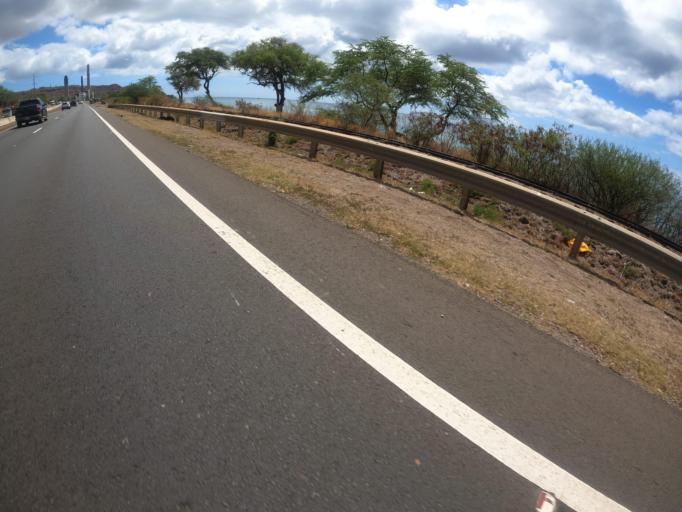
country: US
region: Hawaii
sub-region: Honolulu County
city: Nanakuli
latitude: 21.3651
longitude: -158.1340
